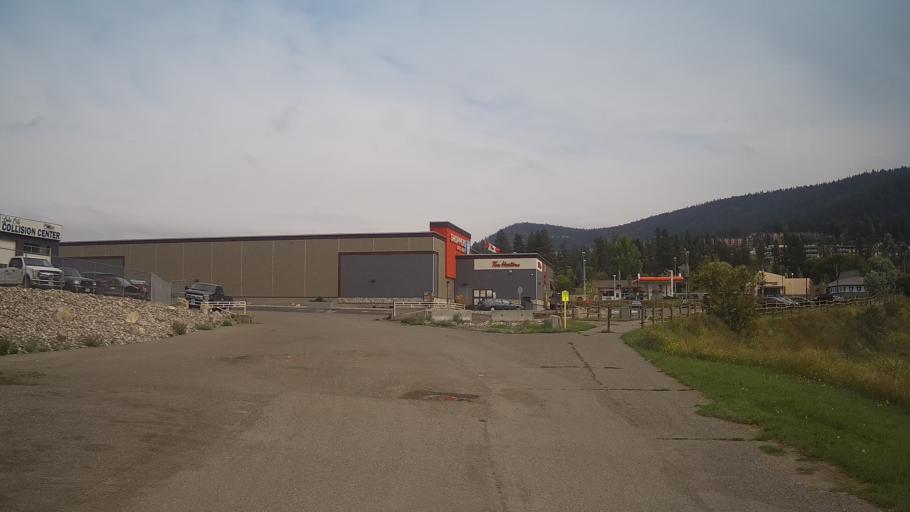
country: CA
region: British Columbia
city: Williams Lake
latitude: 52.1270
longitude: -122.1344
